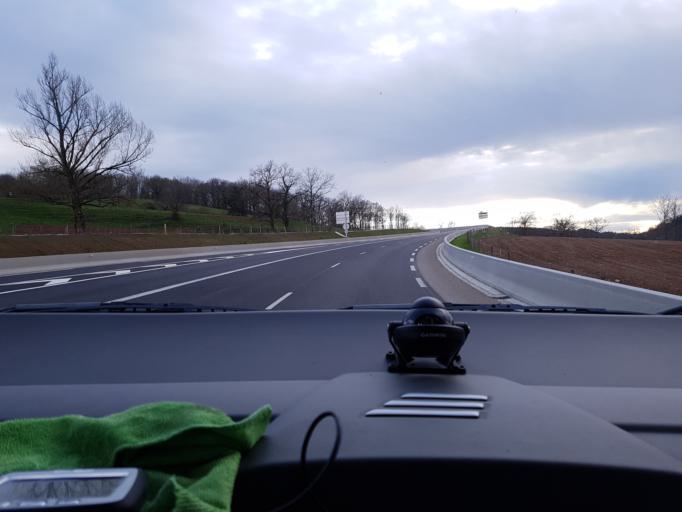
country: FR
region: Midi-Pyrenees
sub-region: Departement de l'Aveyron
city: Espalion
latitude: 44.5269
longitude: 2.7373
